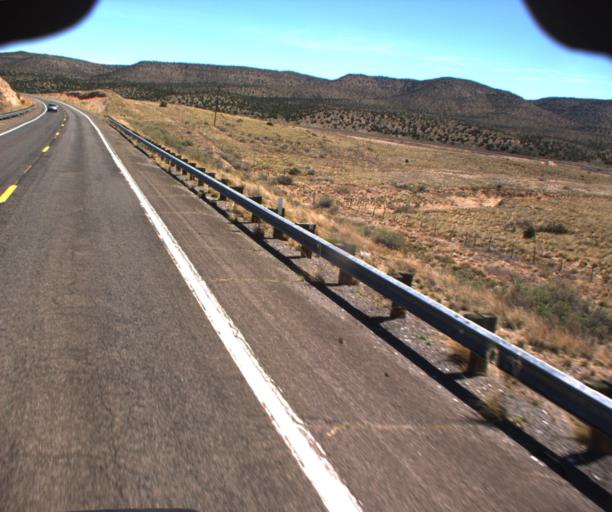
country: US
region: Arizona
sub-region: Mohave County
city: Peach Springs
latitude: 35.5220
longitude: -113.4593
